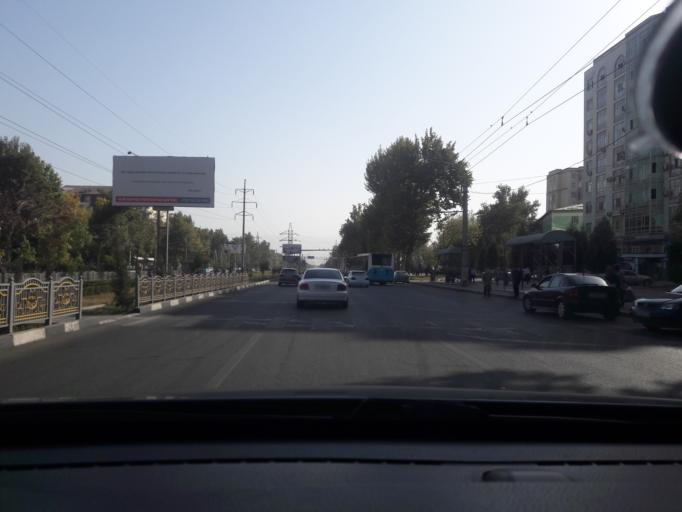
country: TJ
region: Dushanbe
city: Dushanbe
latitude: 38.5271
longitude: 68.7618
